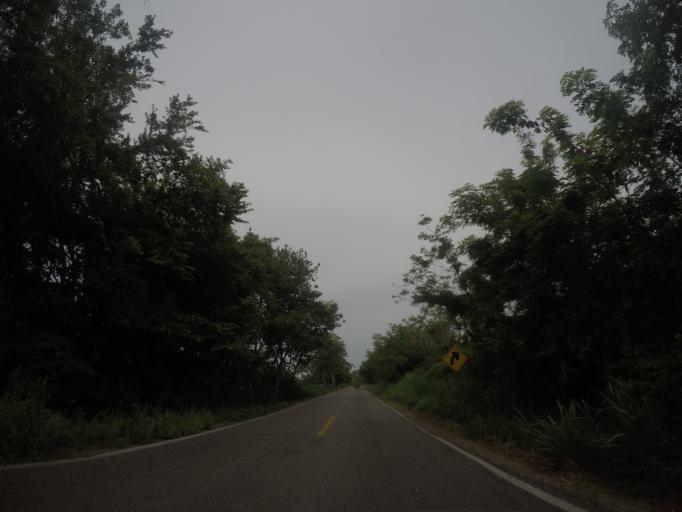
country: MX
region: Oaxaca
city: San Pedro Mixtepec
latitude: 15.9552
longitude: -97.2070
